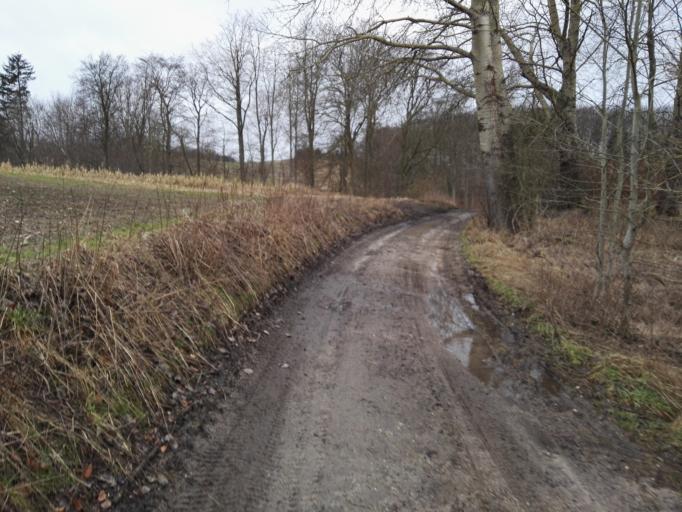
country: DK
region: Zealand
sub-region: Lejre Kommune
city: Lejre
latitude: 55.6398
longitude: 11.9200
